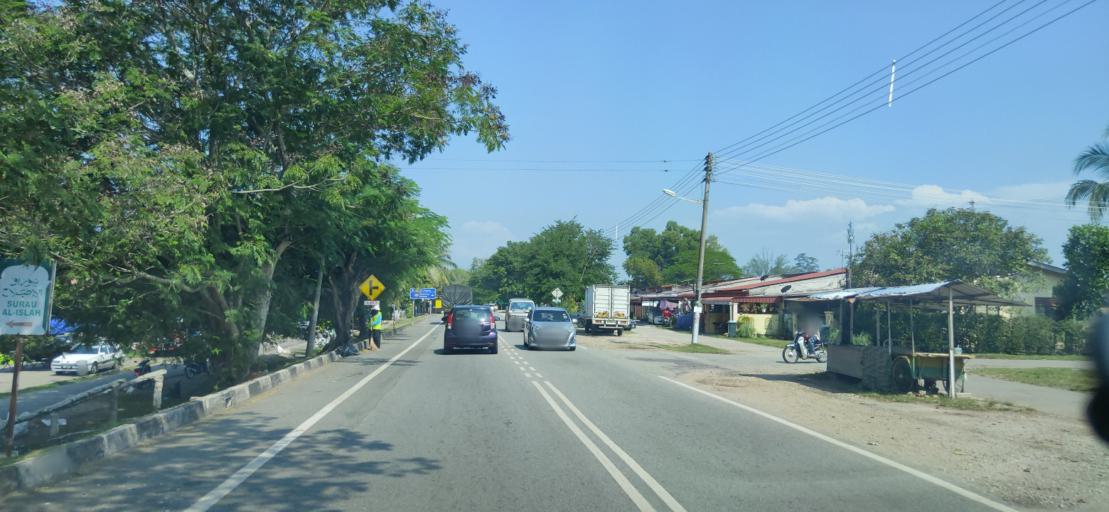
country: MY
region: Kedah
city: Sungai Petani
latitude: 5.6591
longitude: 100.4818
